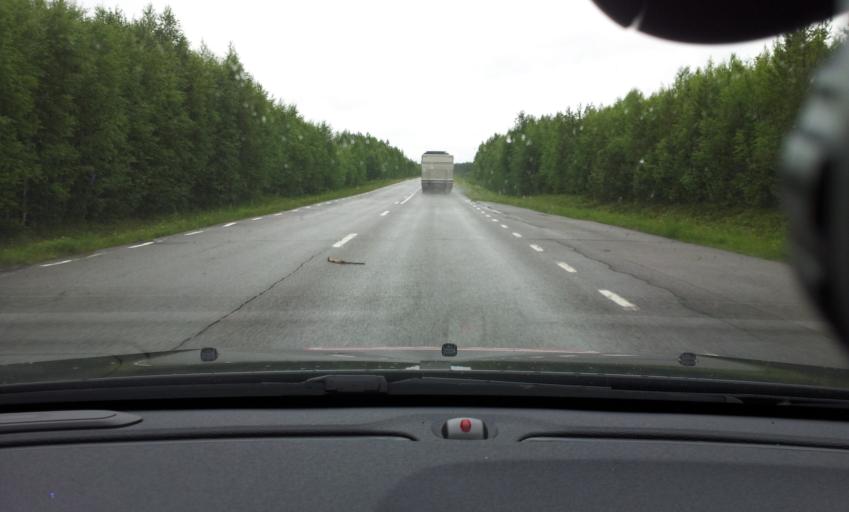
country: SE
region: Jaemtland
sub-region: OEstersunds Kommun
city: Lit
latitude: 63.6461
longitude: 14.6512
